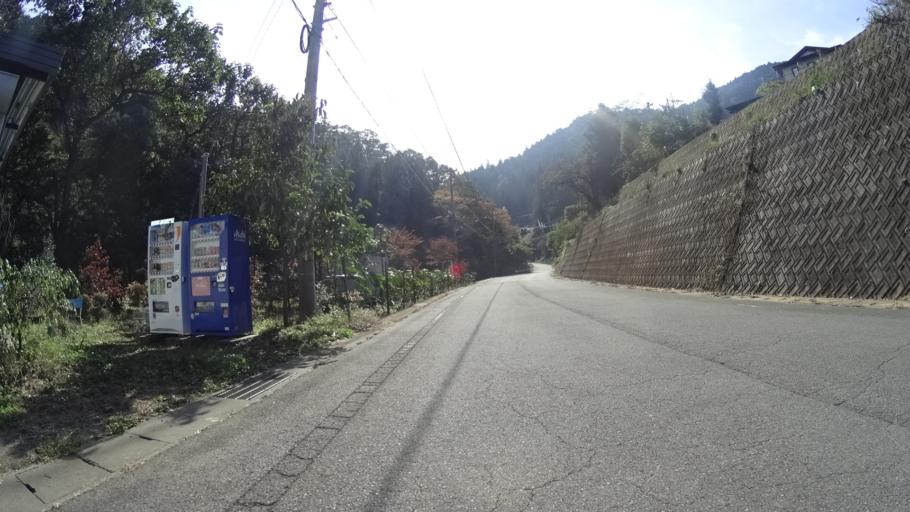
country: JP
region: Yamanashi
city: Otsuki
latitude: 35.5882
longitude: 138.9641
